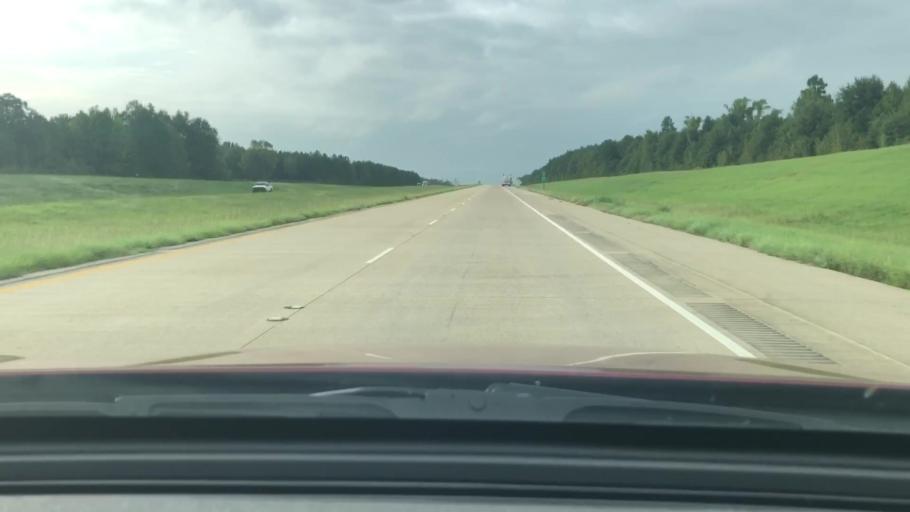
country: US
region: Louisiana
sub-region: Caddo Parish
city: Blanchard
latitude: 32.6151
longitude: -93.8351
